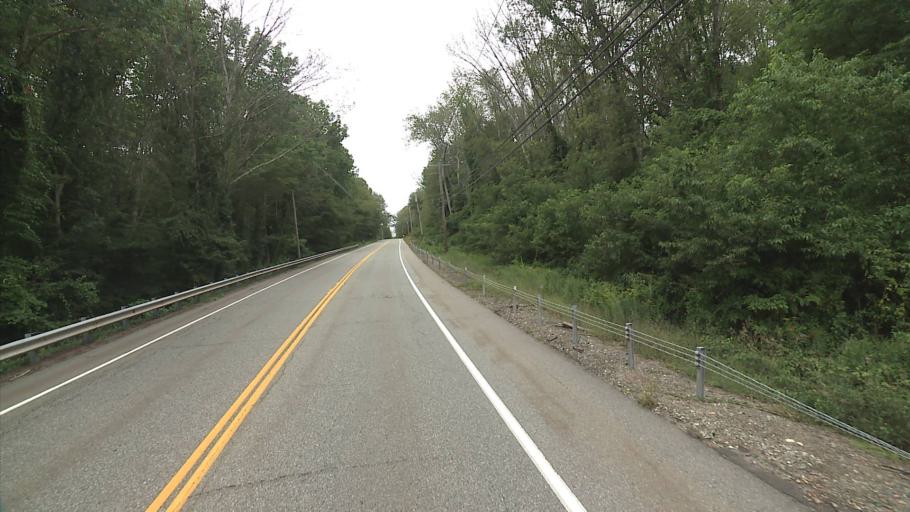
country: US
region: Connecticut
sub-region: Hartford County
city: Terramuggus
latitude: 41.6887
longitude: -72.4284
